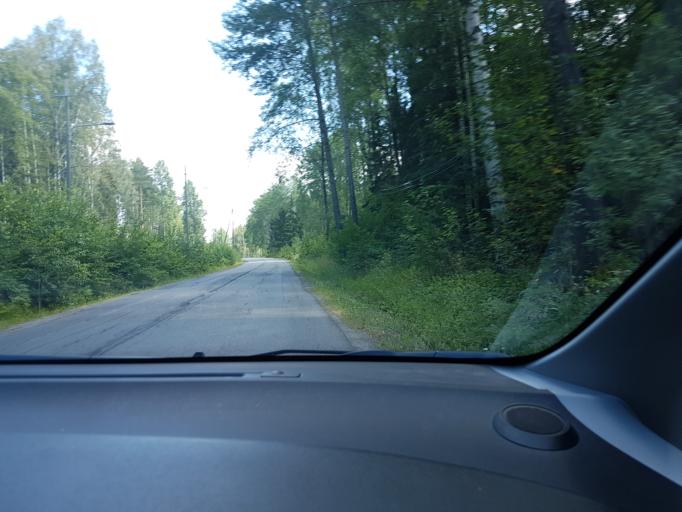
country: FI
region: Uusimaa
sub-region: Helsinki
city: Kilo
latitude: 60.3315
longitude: 24.7754
